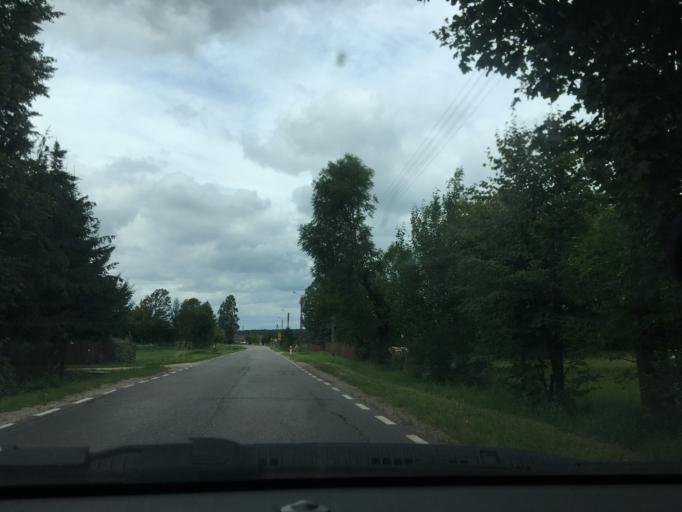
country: PL
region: Podlasie
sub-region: Powiat suwalski
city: Raczki
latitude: 53.9561
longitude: 22.8250
